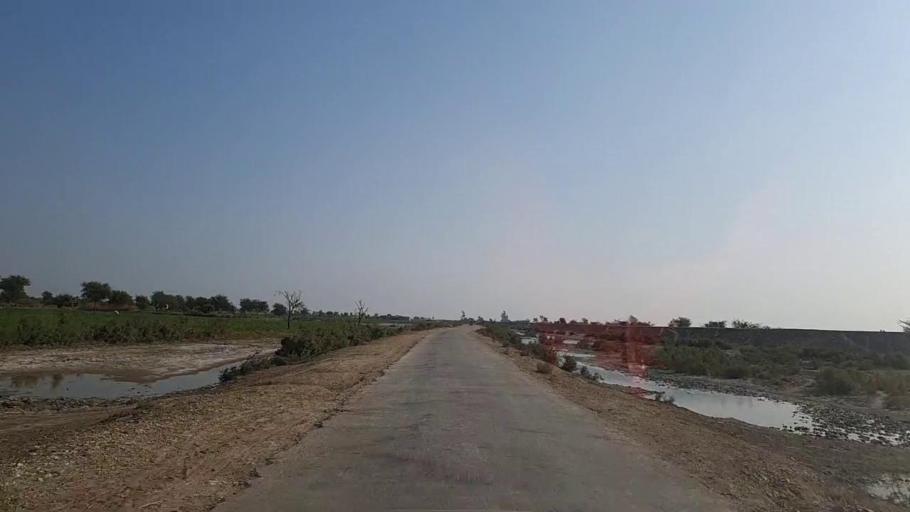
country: PK
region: Sindh
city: Sanghar
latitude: 25.9609
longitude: 69.0391
